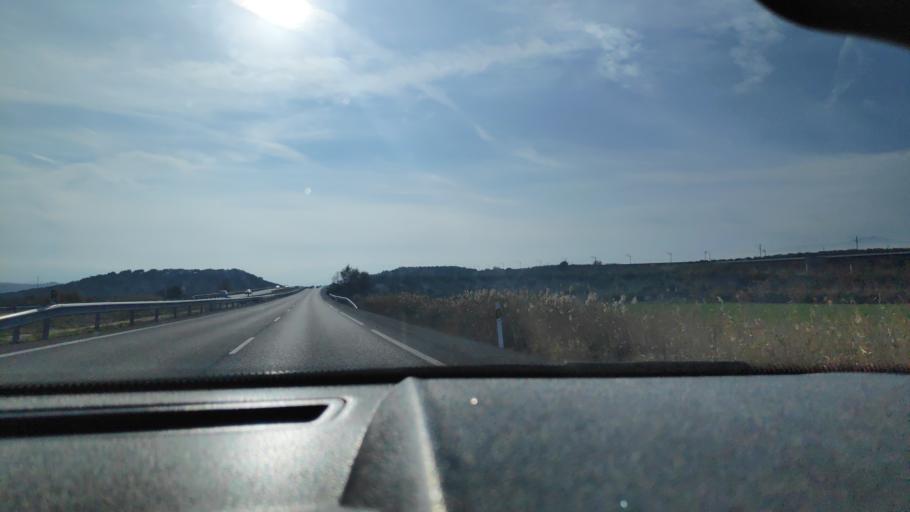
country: ES
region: Andalusia
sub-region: Provincia de Jaen
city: Mengibar
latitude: 37.8772
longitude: -3.7694
